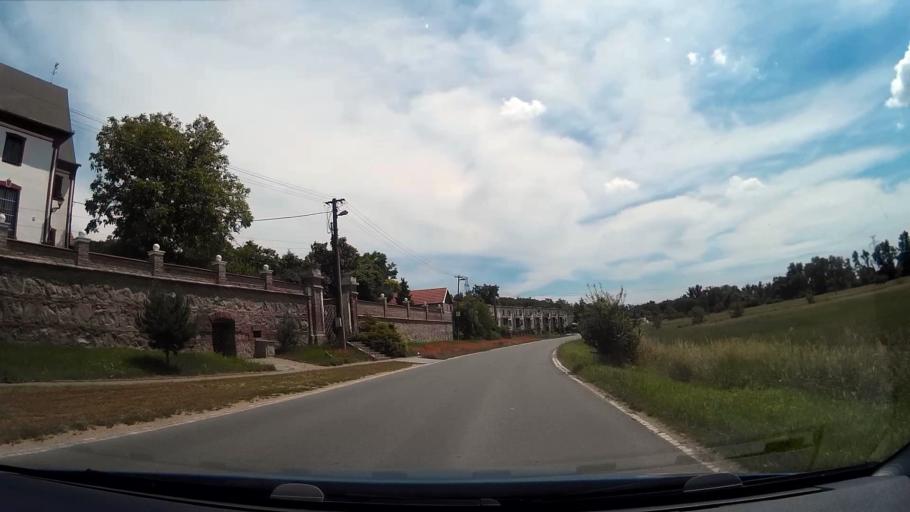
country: CZ
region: South Moravian
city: Dolni Kounice
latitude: 49.0538
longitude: 16.4895
